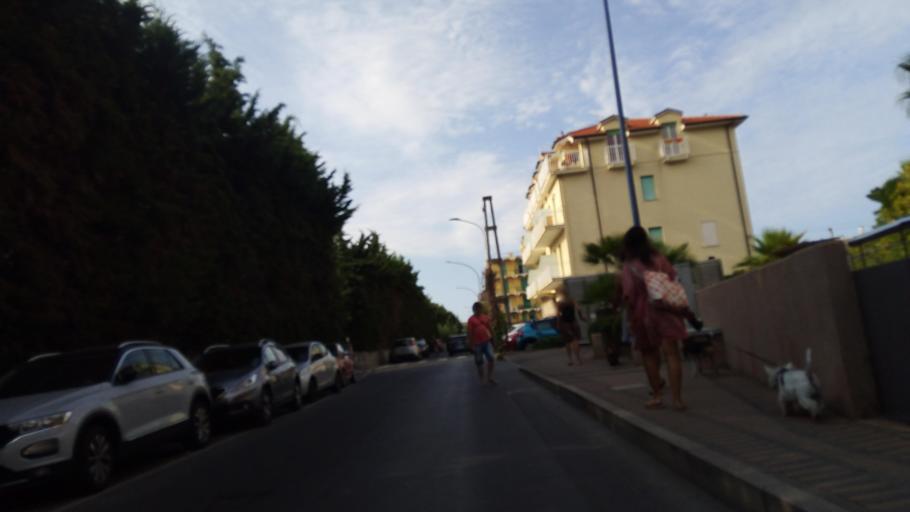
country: IT
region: Liguria
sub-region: Provincia di Savona
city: Ceriale
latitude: 44.0874
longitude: 8.2284
